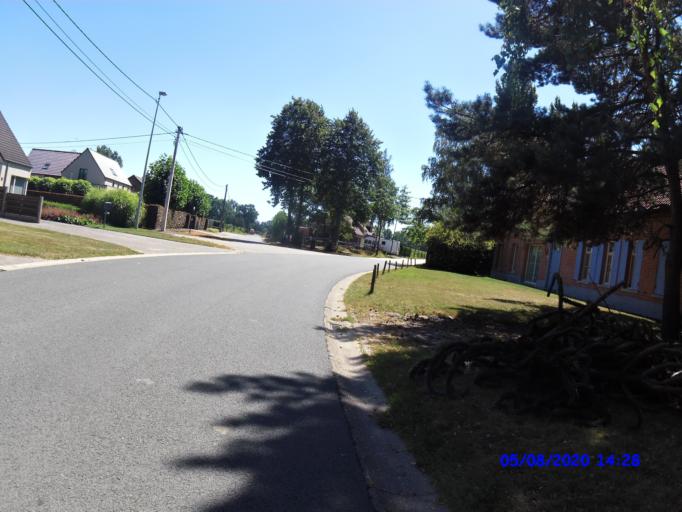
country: BE
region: Flanders
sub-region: Provincie Antwerpen
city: Hoogstraten
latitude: 51.3759
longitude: 4.7694
